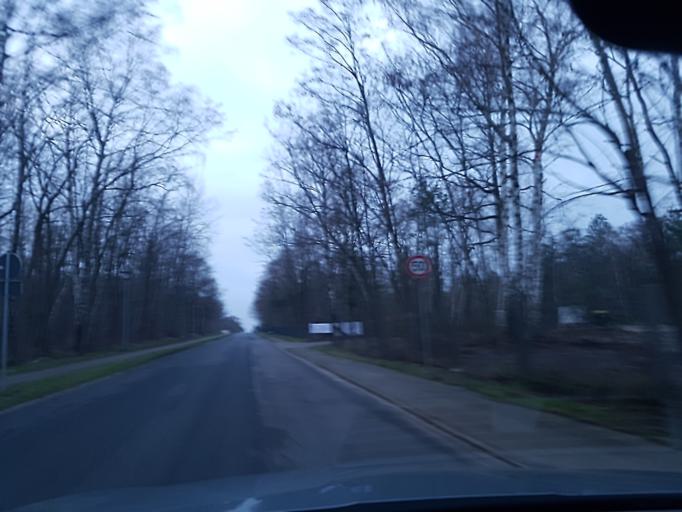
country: DE
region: Brandenburg
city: Schonborn
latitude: 51.6009
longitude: 13.4843
